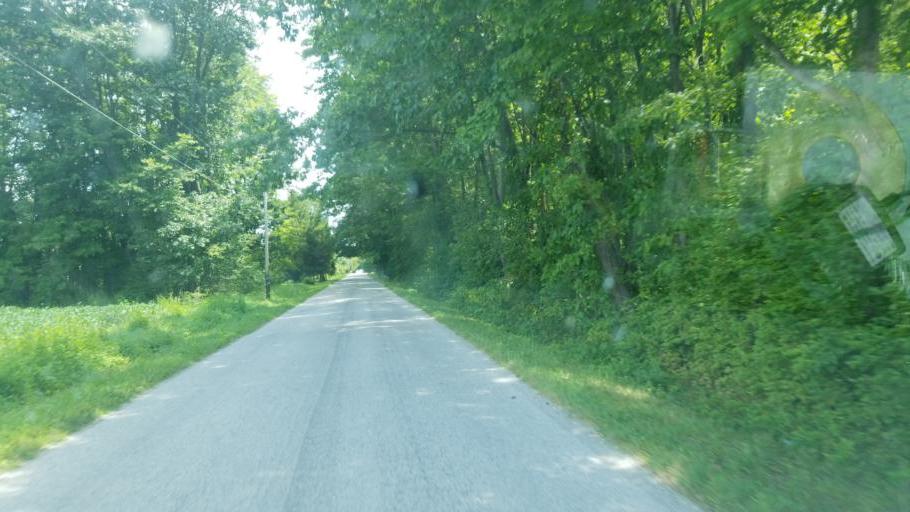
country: US
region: Ohio
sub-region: Delaware County
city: Sunbury
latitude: 40.3378
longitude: -82.8087
